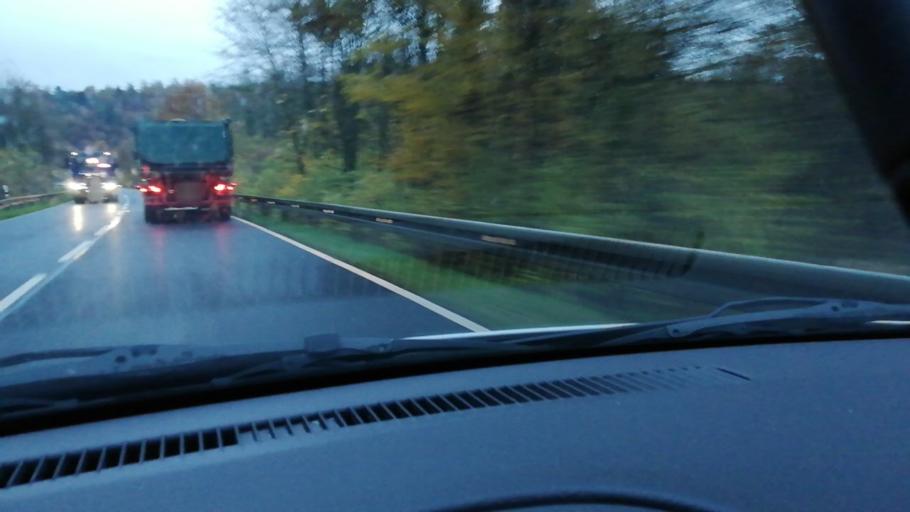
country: DE
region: Bavaria
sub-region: Regierungsbezirk Unterfranken
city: Hosbach
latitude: 50.0410
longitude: 9.1991
